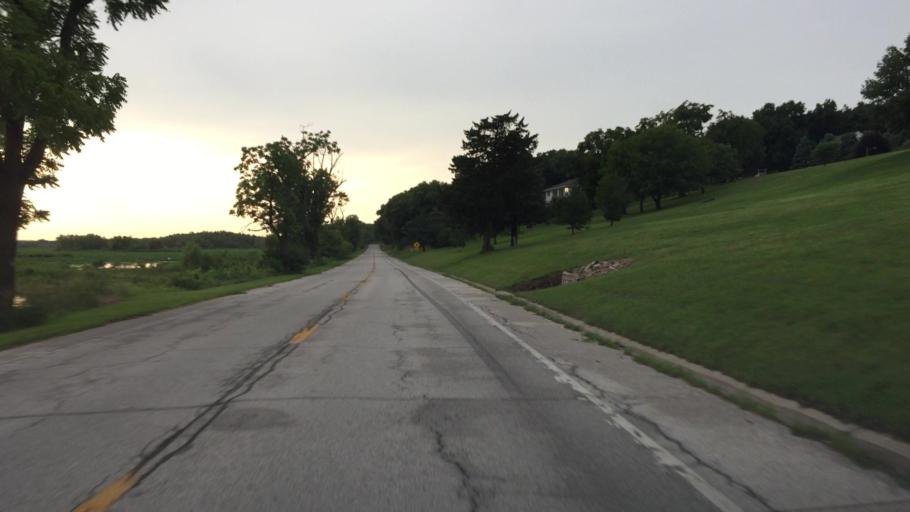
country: US
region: Illinois
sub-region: Hancock County
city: Nauvoo
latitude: 40.5279
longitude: -91.3703
